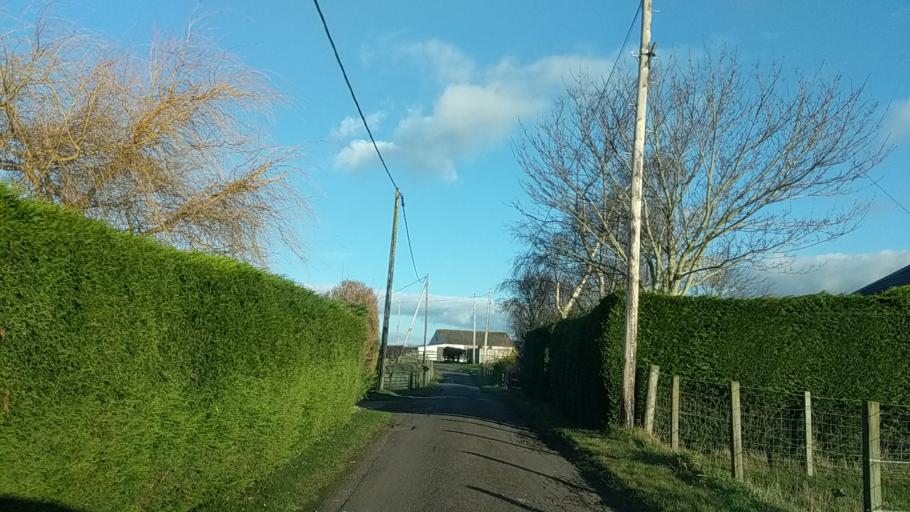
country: GB
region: Scotland
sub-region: West Lothian
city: Linlithgow
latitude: 55.9916
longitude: -3.5430
